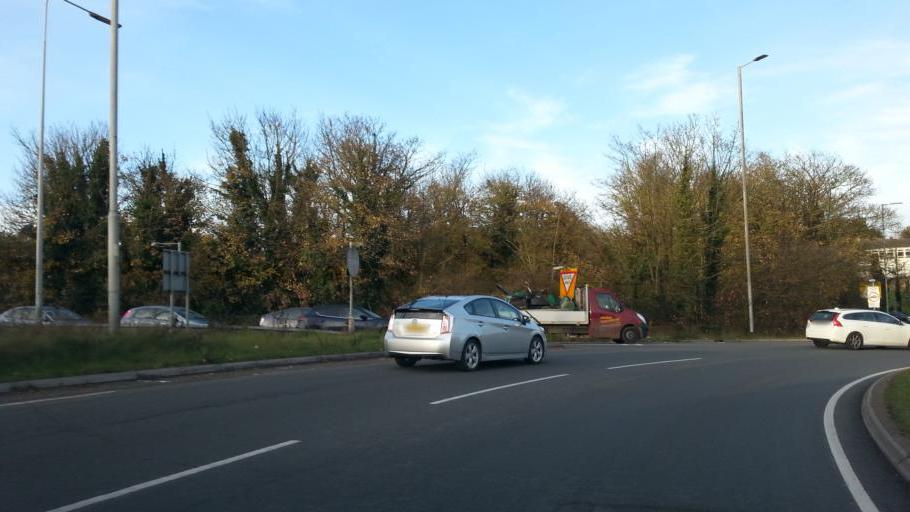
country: GB
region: England
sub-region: Hertfordshire
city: St Albans
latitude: 51.7326
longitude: -0.3451
